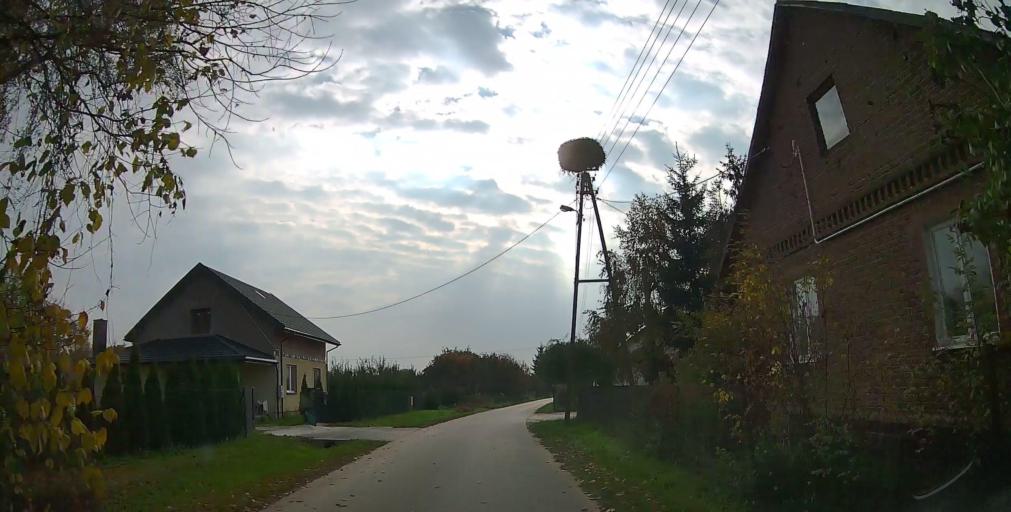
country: PL
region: Masovian Voivodeship
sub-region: Powiat grojecki
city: Mogielnica
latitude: 51.6409
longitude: 20.7447
